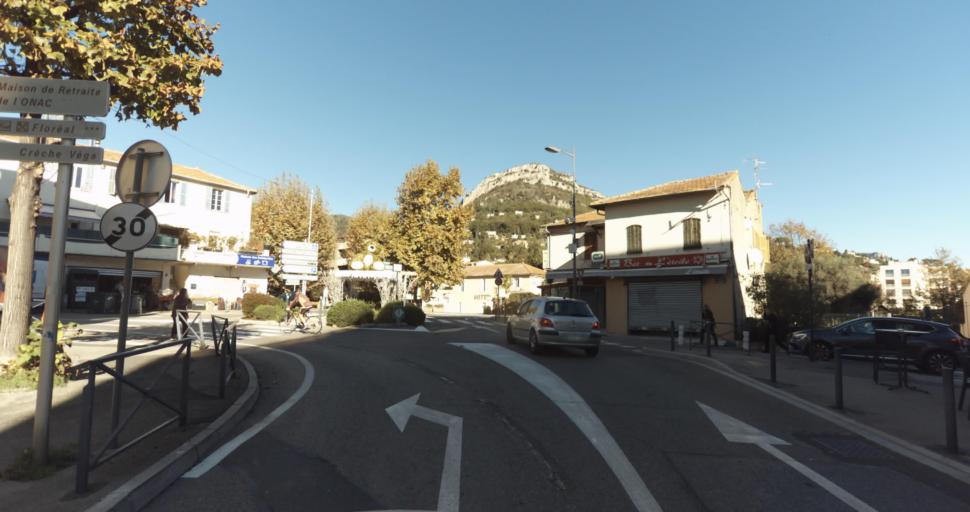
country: FR
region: Provence-Alpes-Cote d'Azur
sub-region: Departement des Alpes-Maritimes
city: Vence
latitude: 43.7243
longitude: 7.1072
